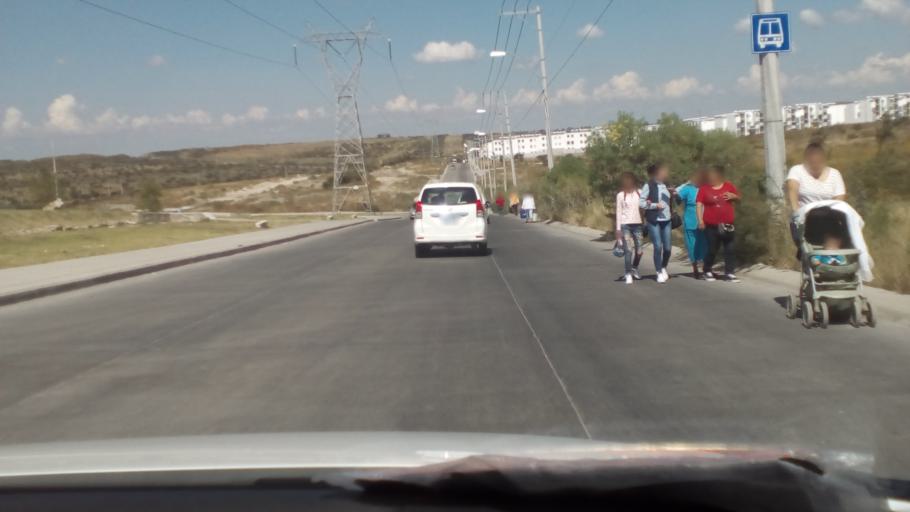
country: MX
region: Guanajuato
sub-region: Leon
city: Fraccionamiento Paseo de las Torres
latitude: 21.1715
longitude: -101.7627
